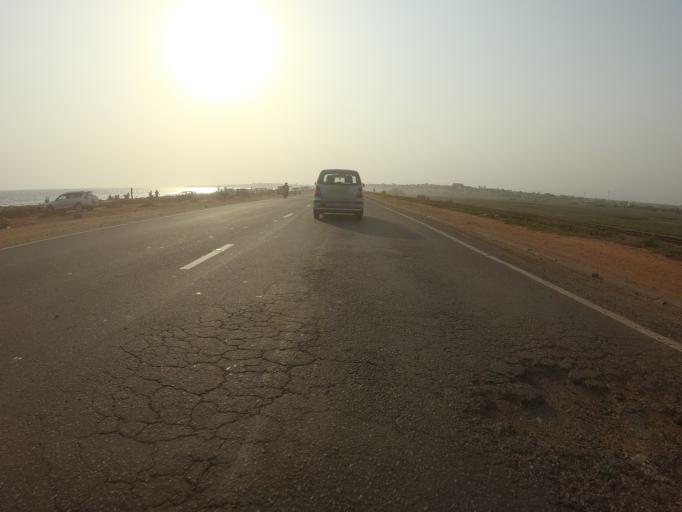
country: GH
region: Greater Accra
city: Nungua
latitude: 5.6130
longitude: -0.0377
